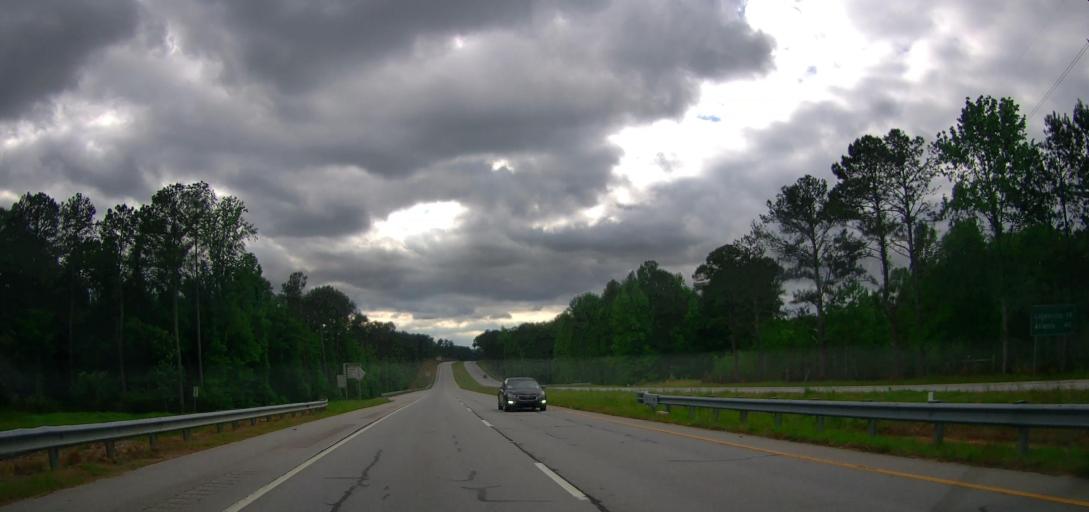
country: US
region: Georgia
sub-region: Walton County
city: Monroe
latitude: 33.8020
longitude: -83.7378
